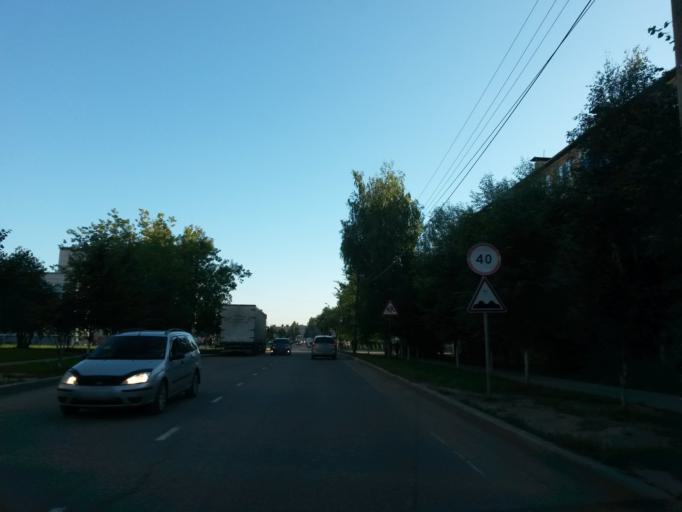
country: RU
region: Jaroslavl
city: Tutayev
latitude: 57.8676
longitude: 39.5171
